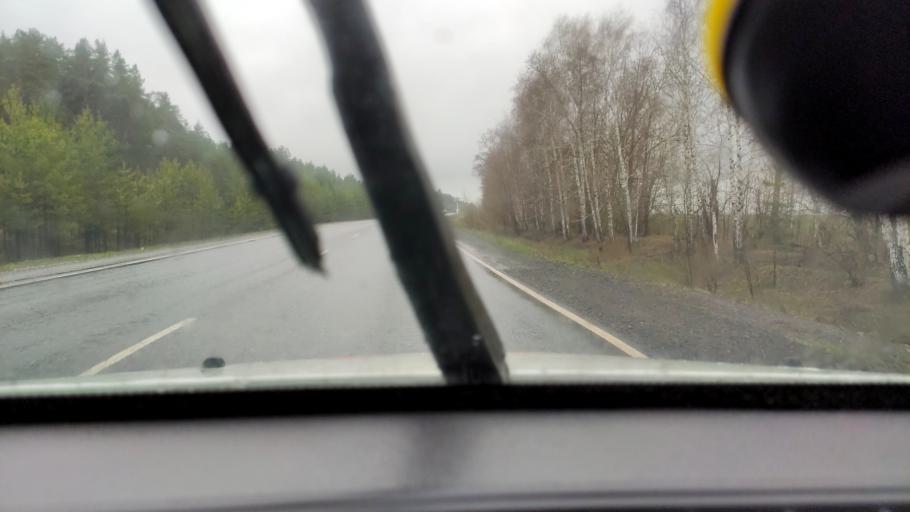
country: RU
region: Samara
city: Povolzhskiy
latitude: 53.6263
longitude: 49.6525
